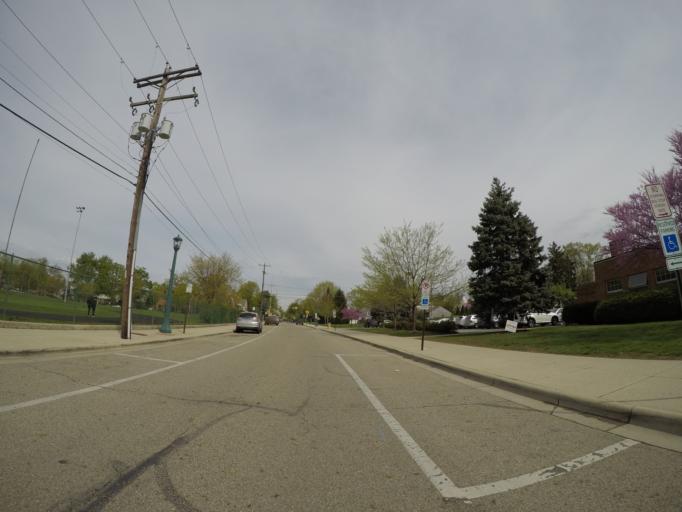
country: US
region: Ohio
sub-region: Franklin County
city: Upper Arlington
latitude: 40.0005
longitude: -83.0575
